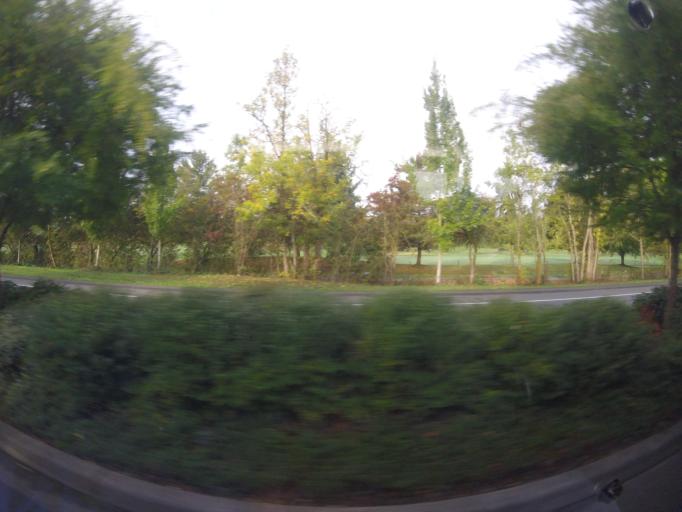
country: US
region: Washington
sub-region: King County
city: Medina
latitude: 47.6228
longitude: -122.2280
